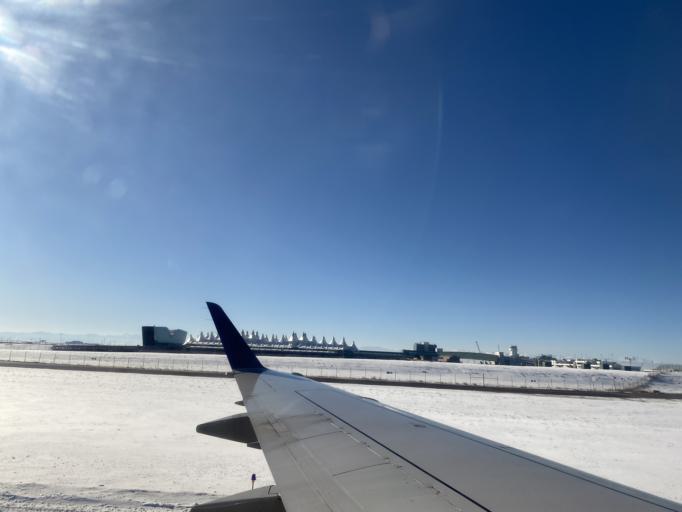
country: US
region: Colorado
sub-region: Weld County
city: Lochbuie
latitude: 39.8503
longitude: -104.6624
